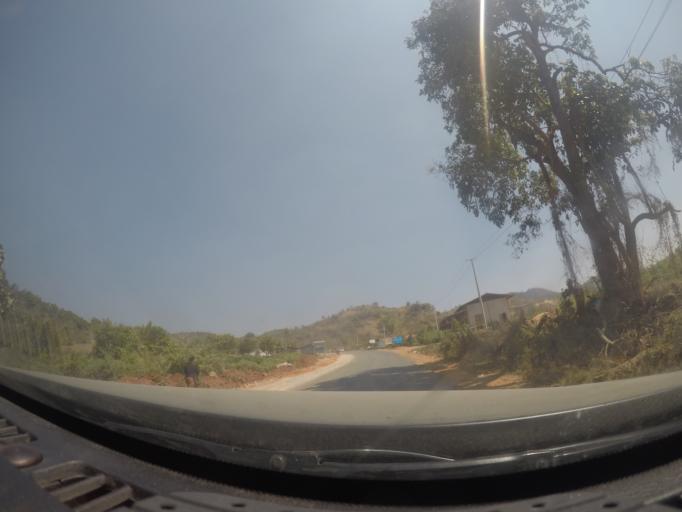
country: MM
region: Shan
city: Taunggyi
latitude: 20.8088
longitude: 97.2724
